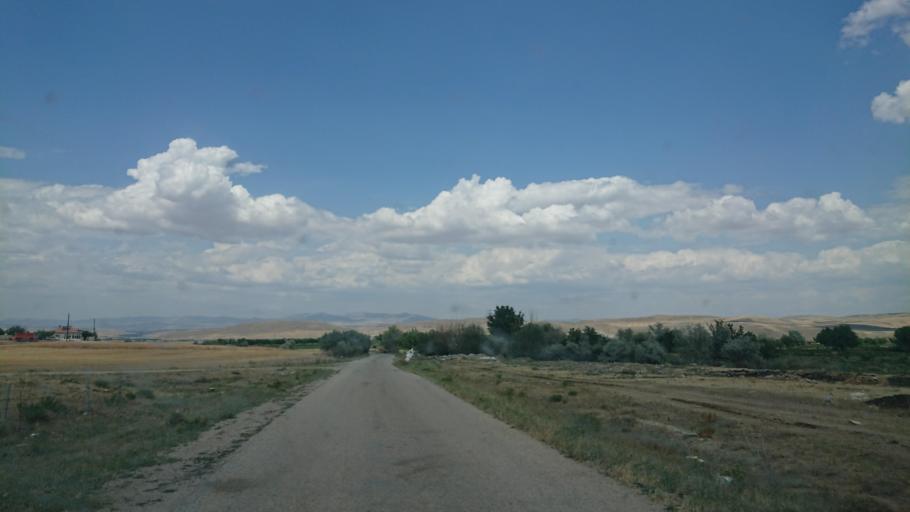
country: TR
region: Aksaray
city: Sariyahsi
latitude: 38.9659
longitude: 33.8902
